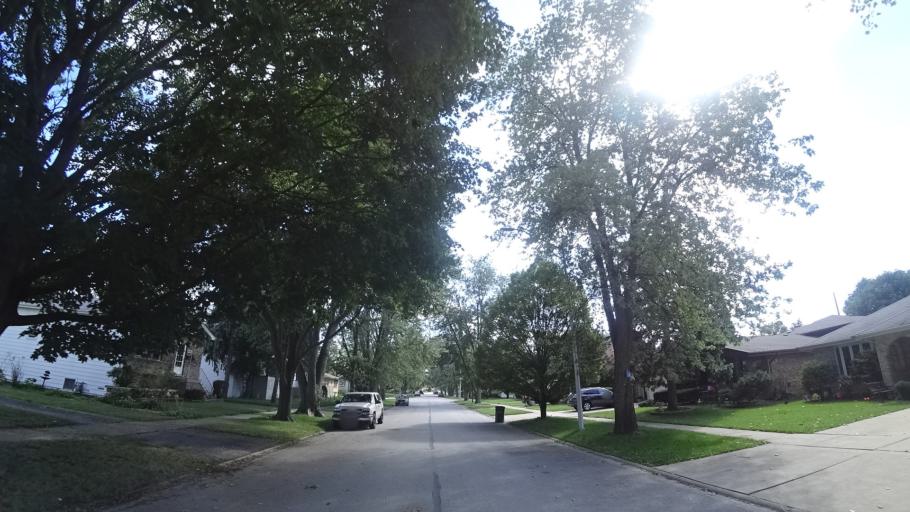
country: US
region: Illinois
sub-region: Cook County
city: Oak Lawn
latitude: 41.7223
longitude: -87.7580
